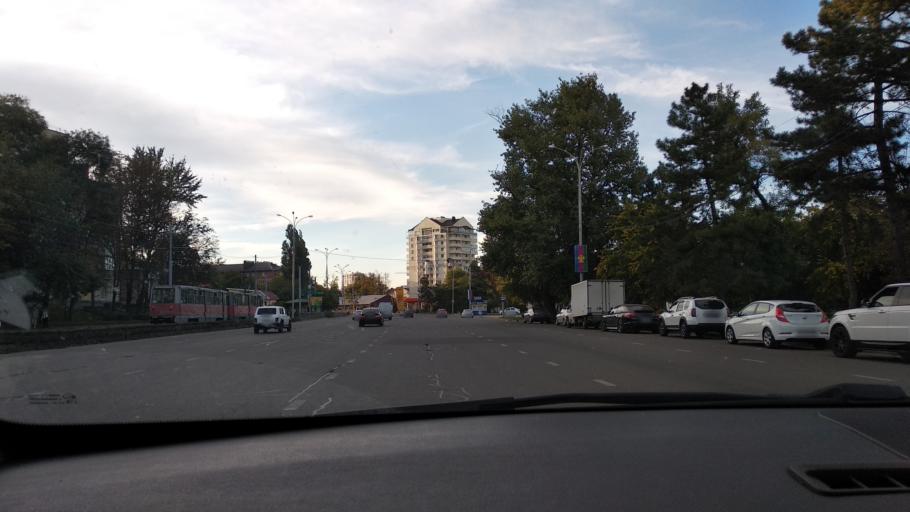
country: RU
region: Krasnodarskiy
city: Krasnodar
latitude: 45.0237
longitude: 38.9958
